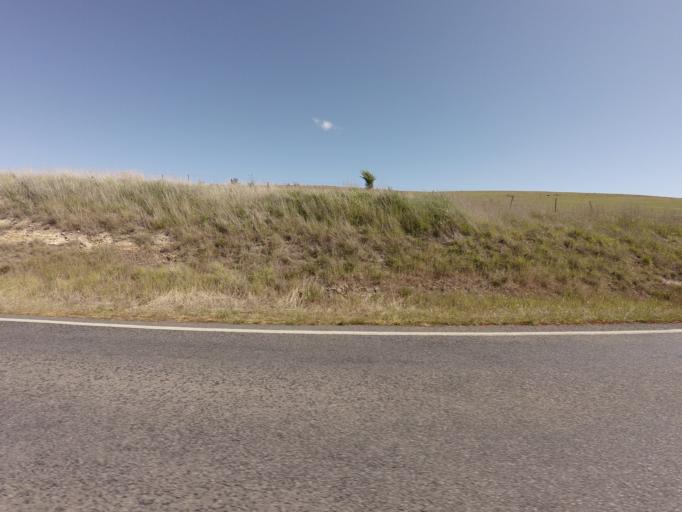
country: AU
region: Tasmania
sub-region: Derwent Valley
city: New Norfolk
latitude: -42.6508
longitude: 146.9313
